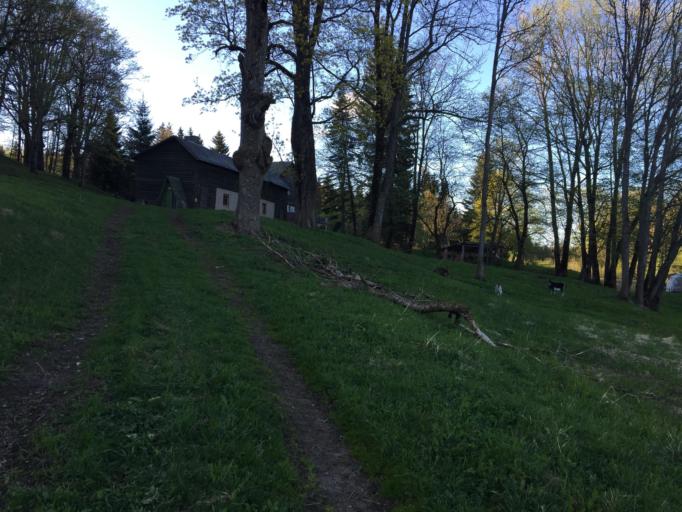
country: LV
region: Vecpiebalga
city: Vecpiebalga
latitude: 56.8701
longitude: 25.9649
